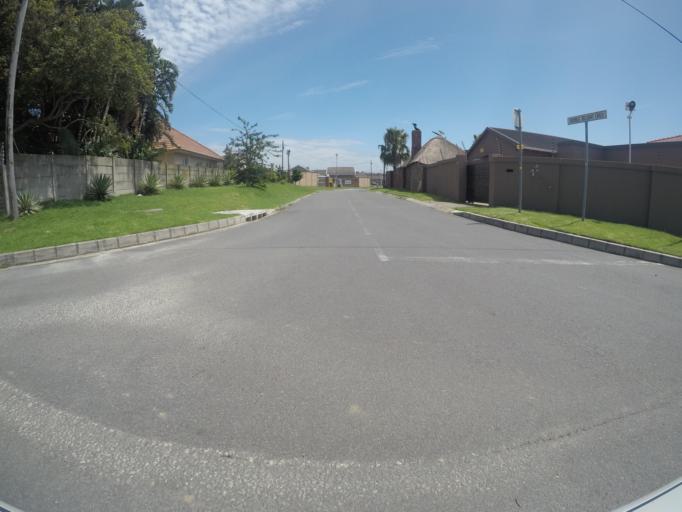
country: ZA
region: Eastern Cape
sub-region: Buffalo City Metropolitan Municipality
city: East London
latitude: -32.9499
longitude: 27.9996
